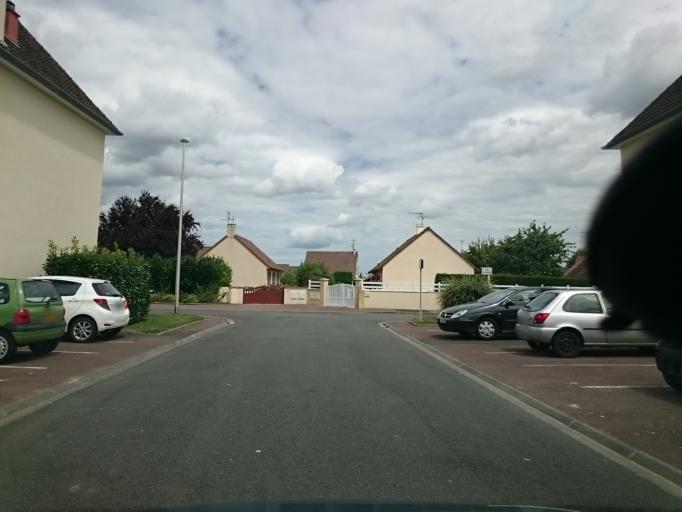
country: FR
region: Lower Normandy
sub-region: Departement du Calvados
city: Cormelles-le-Royal
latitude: 49.1587
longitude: -0.3333
